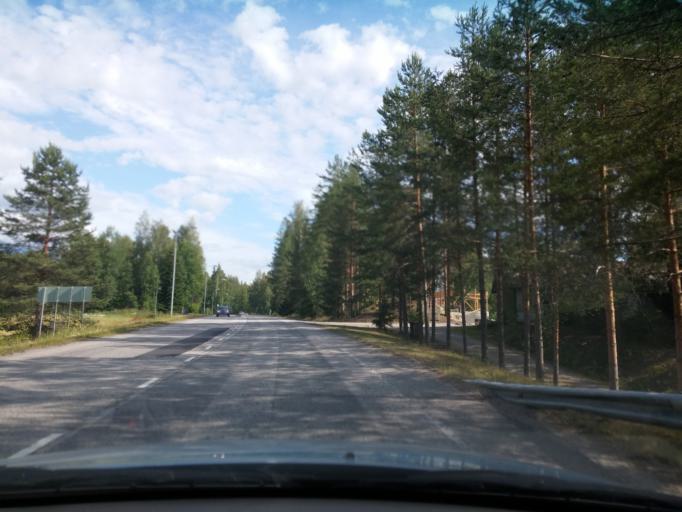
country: FI
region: Central Finland
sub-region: Keuruu
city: Keuruu
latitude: 62.2688
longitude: 24.6923
